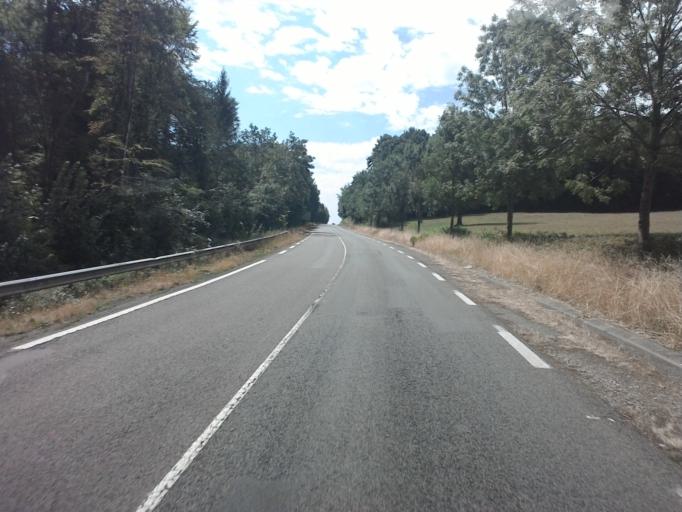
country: FR
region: Bourgogne
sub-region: Departement de Saone-et-Loire
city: Cuiseaux
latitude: 46.4783
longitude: 5.3632
